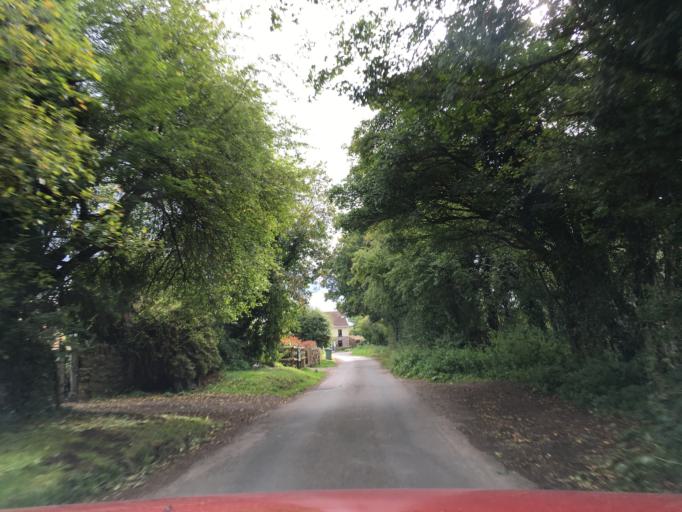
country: GB
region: England
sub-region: South Gloucestershire
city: Wickwar
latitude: 51.5932
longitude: -2.4153
